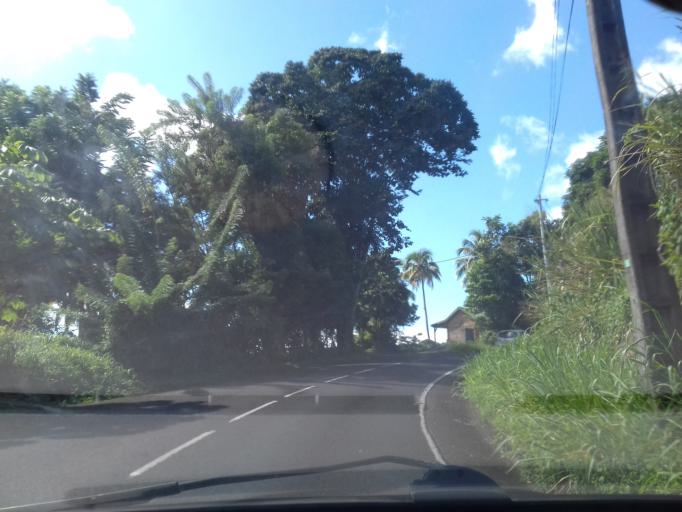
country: MQ
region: Martinique
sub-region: Martinique
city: Saint-Joseph
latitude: 14.6559
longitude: -61.0472
